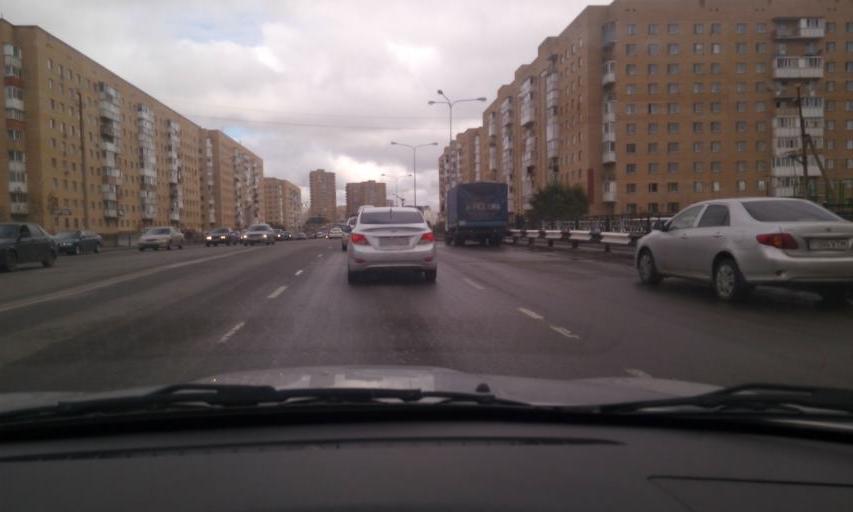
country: KZ
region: Astana Qalasy
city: Astana
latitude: 51.1715
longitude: 71.3820
